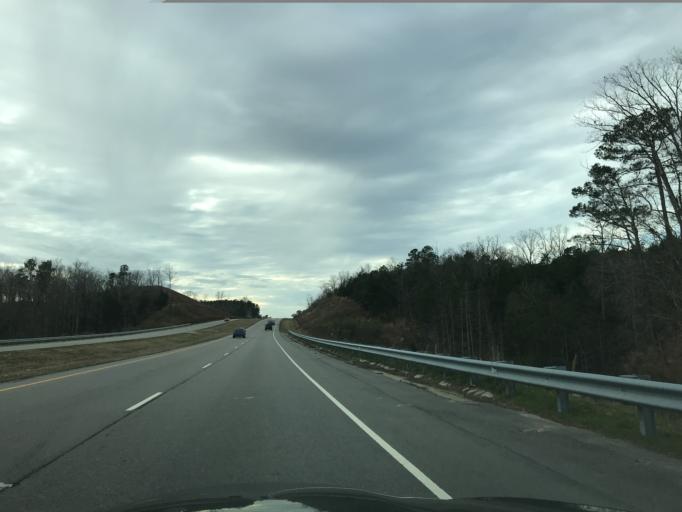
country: US
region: North Carolina
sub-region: Wake County
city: Rolesville
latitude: 35.9051
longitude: -78.4606
